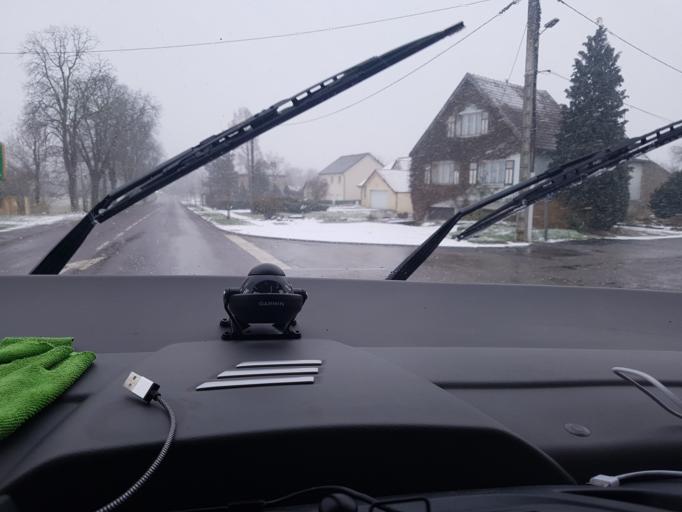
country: FR
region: Lorraine
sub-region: Departement de la Moselle
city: Remilly
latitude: 48.8834
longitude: 6.3970
